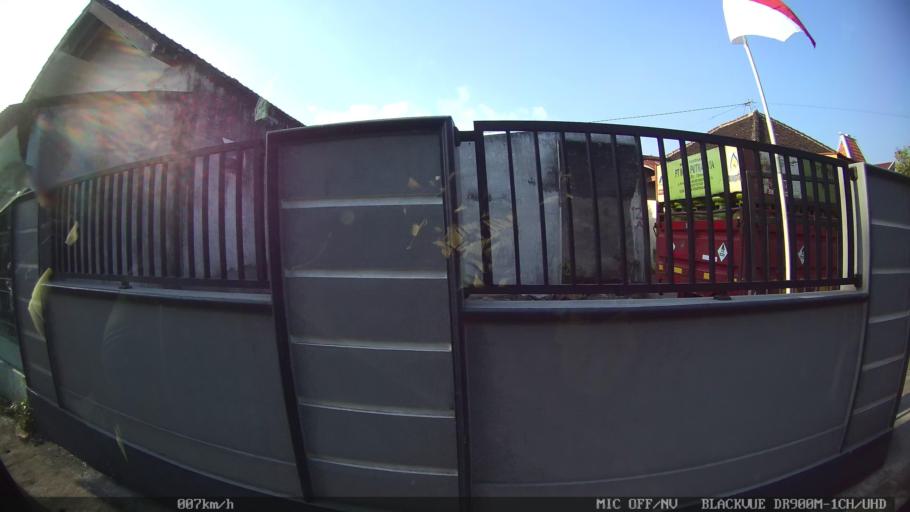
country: ID
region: Daerah Istimewa Yogyakarta
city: Yogyakarta
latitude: -7.8246
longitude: 110.3887
